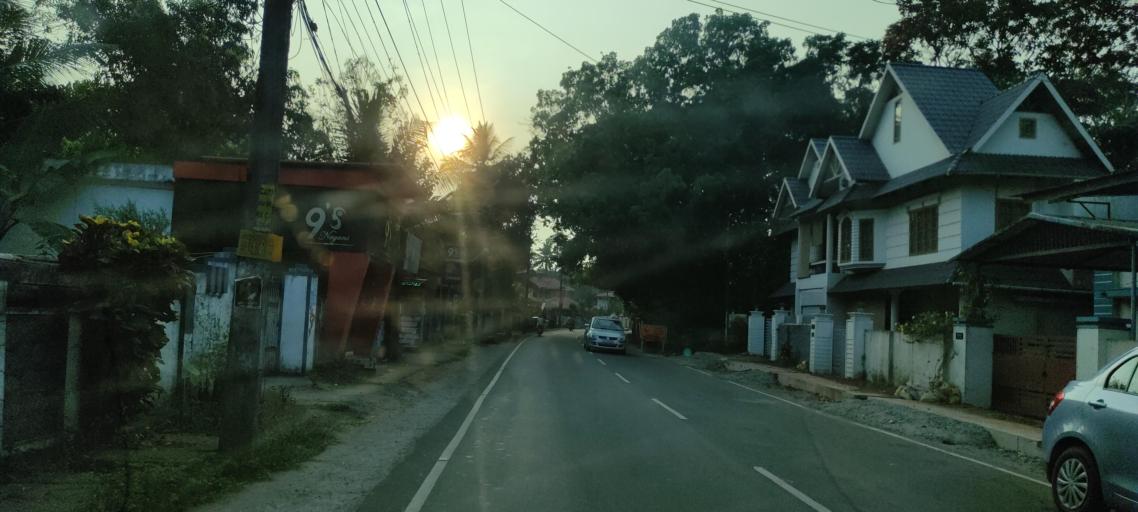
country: IN
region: Kerala
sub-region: Alappuzha
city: Mavelikara
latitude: 9.2549
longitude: 76.5641
